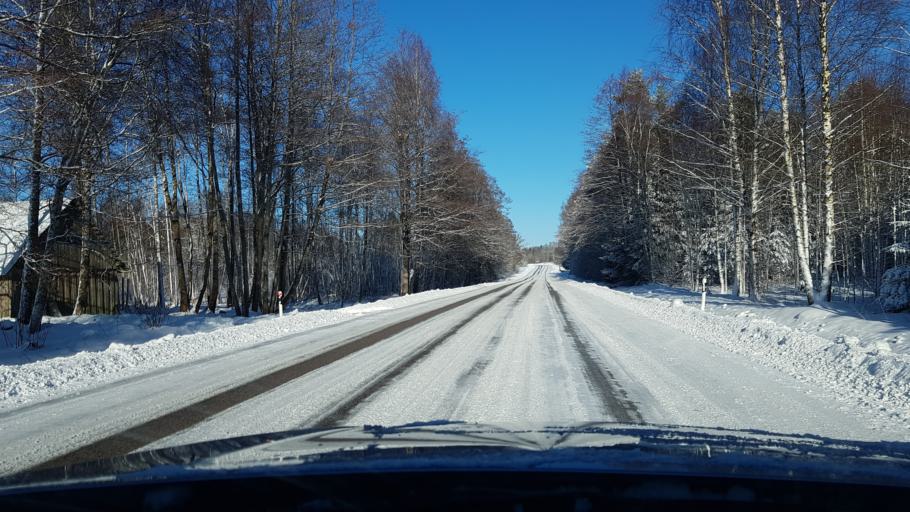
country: EE
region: Hiiumaa
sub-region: Kaerdla linn
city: Kardla
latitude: 58.9131
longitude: 22.7929
